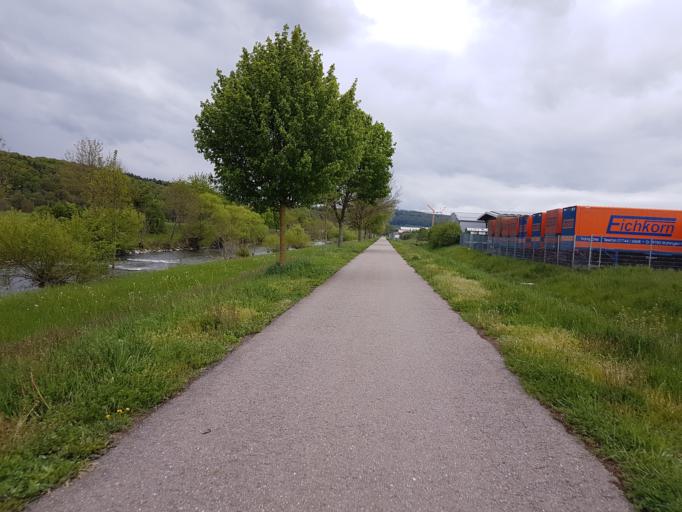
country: DE
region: Baden-Wuerttemberg
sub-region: Freiburg Region
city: Wutoschingen
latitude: 47.6423
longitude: 8.3493
